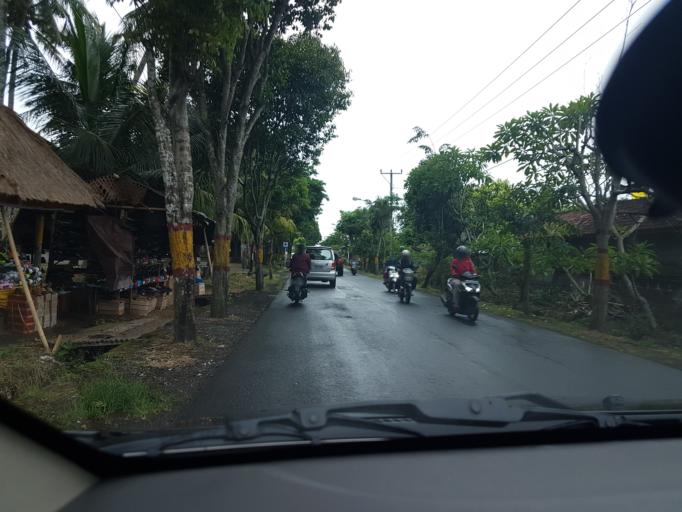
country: ID
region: Bali
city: Banjar Sedang
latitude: -8.5751
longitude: 115.2383
